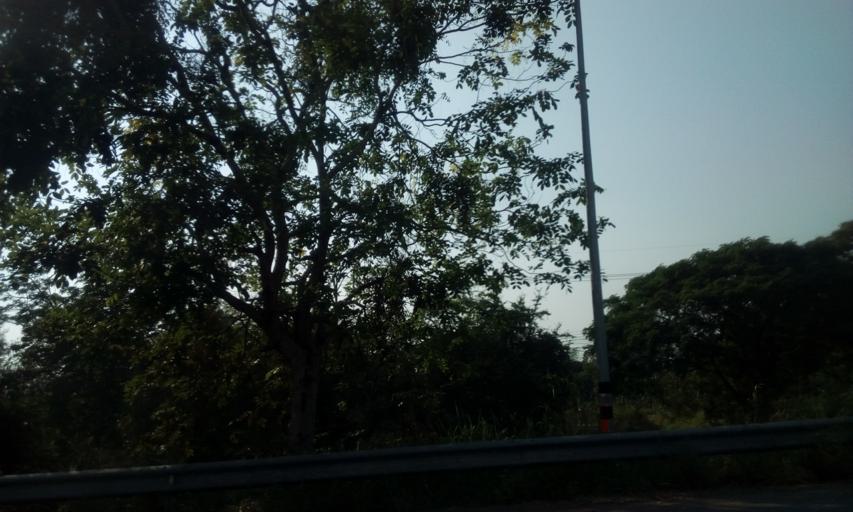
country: TH
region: Sing Buri
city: Phrom Buri
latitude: 14.7815
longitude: 100.4339
